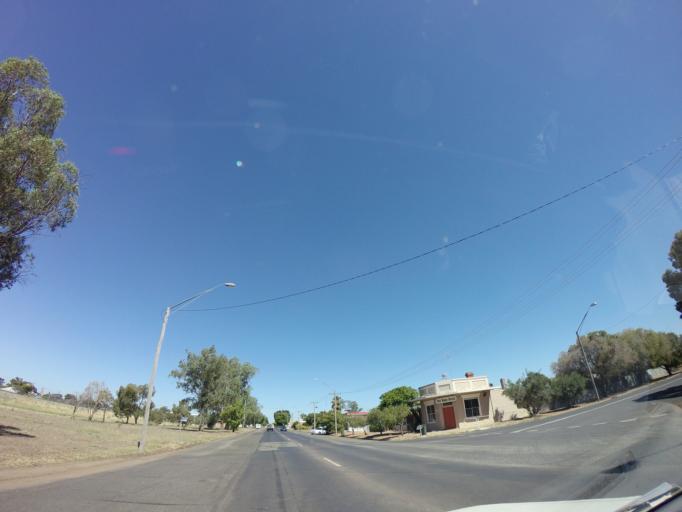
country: AU
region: New South Wales
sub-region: Bogan
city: Nyngan
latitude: -31.5603
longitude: 147.1910
